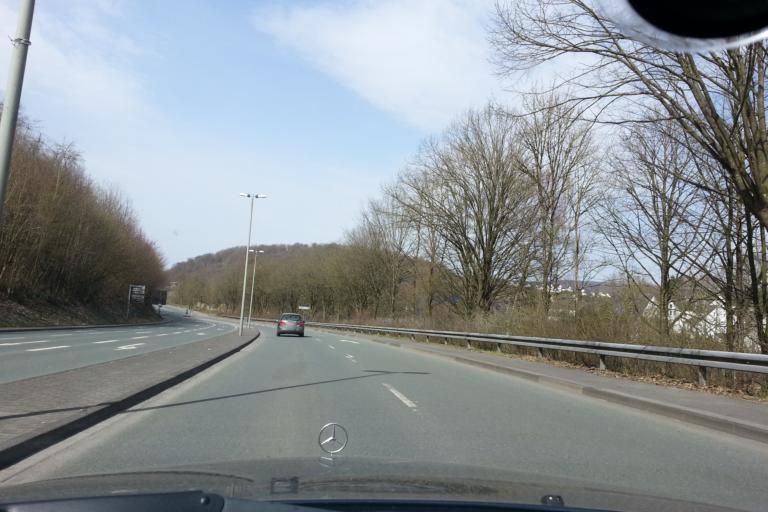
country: DE
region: North Rhine-Westphalia
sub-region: Regierungsbezirk Arnsberg
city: Meschede
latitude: 51.3486
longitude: 8.2757
